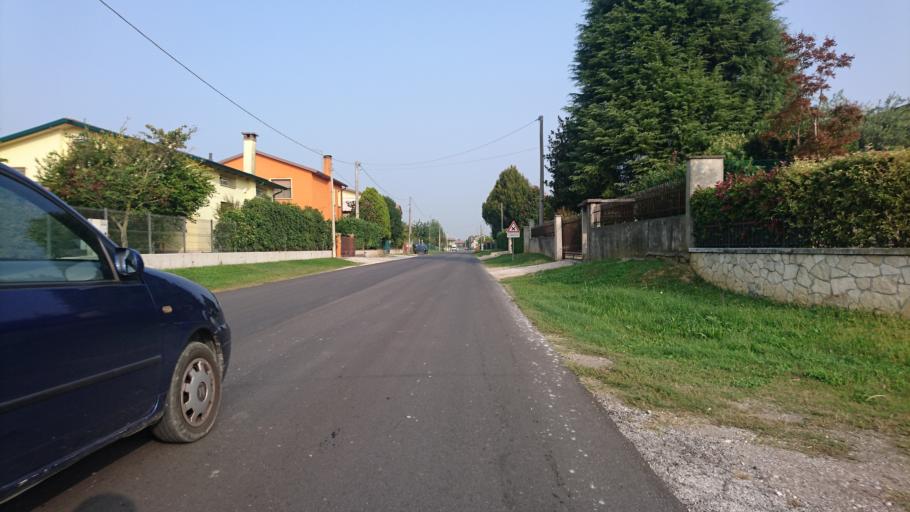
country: IT
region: Veneto
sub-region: Provincia di Padova
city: Curtarolo
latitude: 45.5310
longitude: 11.8407
